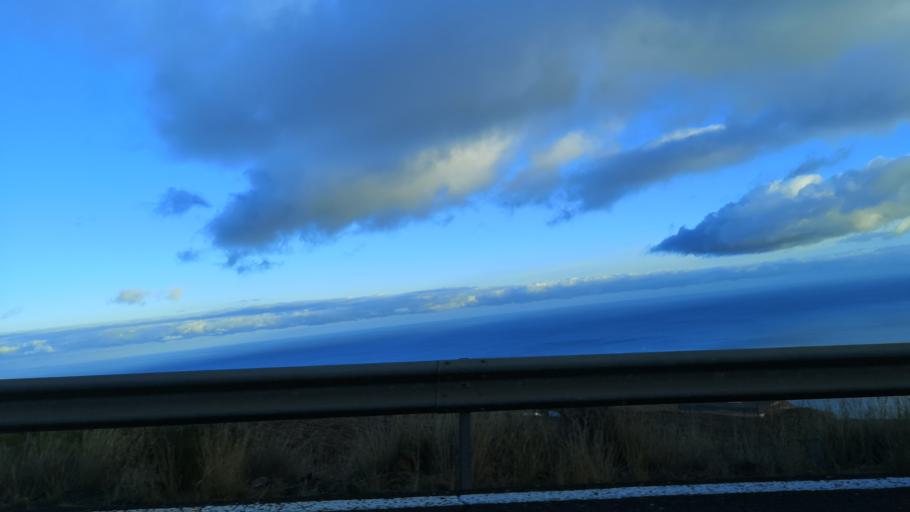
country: ES
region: Canary Islands
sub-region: Provincia de Santa Cruz de Tenerife
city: Alajero
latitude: 28.0411
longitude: -17.2321
